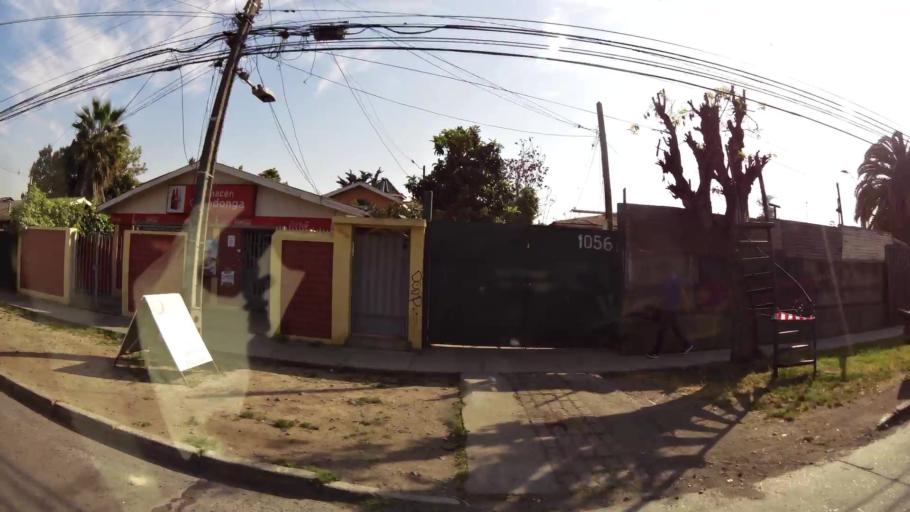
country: CL
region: Santiago Metropolitan
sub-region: Provincia de Maipo
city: San Bernardo
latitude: -33.5930
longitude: -70.7126
